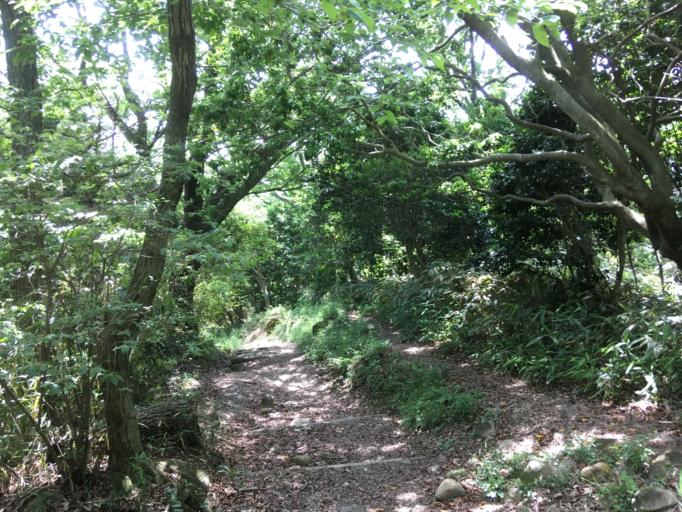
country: JP
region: Nara
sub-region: Ikoma-shi
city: Ikoma
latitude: 34.6568
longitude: 135.6687
